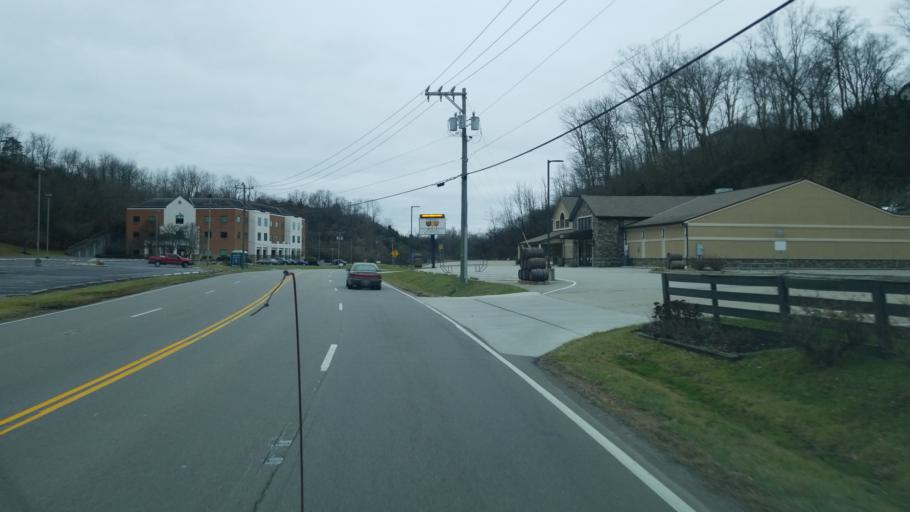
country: US
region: Kentucky
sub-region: Campbell County
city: Southgate
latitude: 39.0645
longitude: -84.4603
